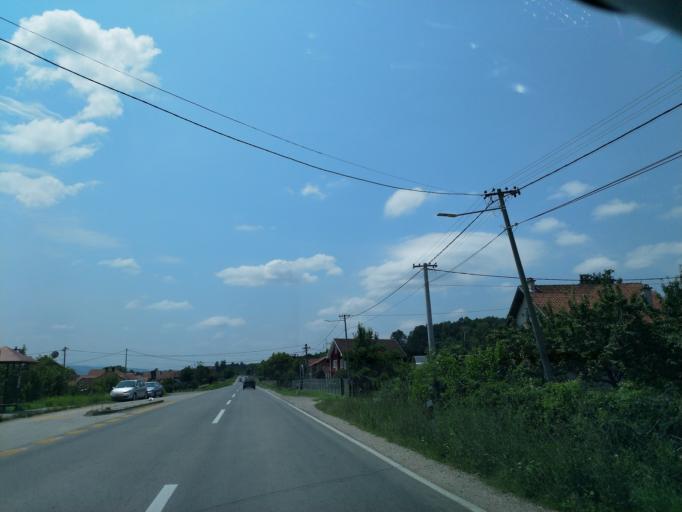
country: RS
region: Central Serbia
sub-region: Rasinski Okrug
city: Krusevac
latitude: 43.5328
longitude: 21.3212
